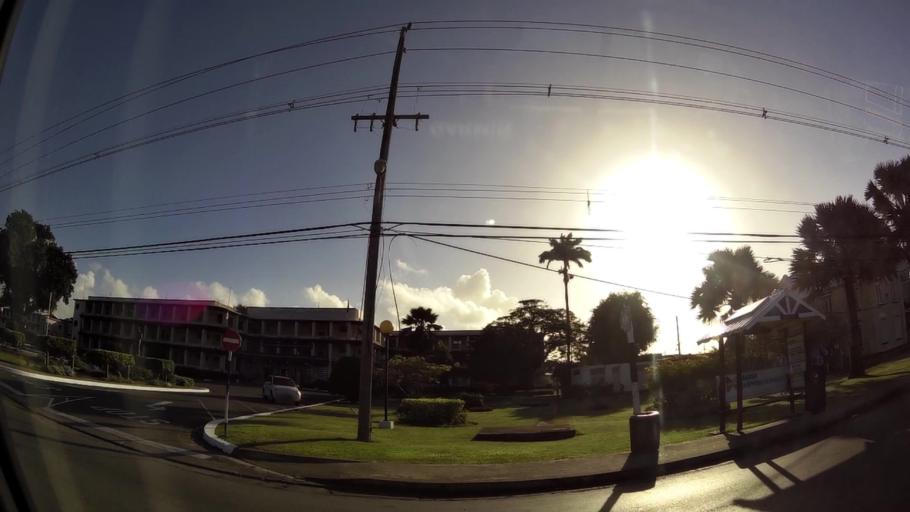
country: BB
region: Saint Michael
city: Bridgetown
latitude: 13.0864
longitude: -59.6092
